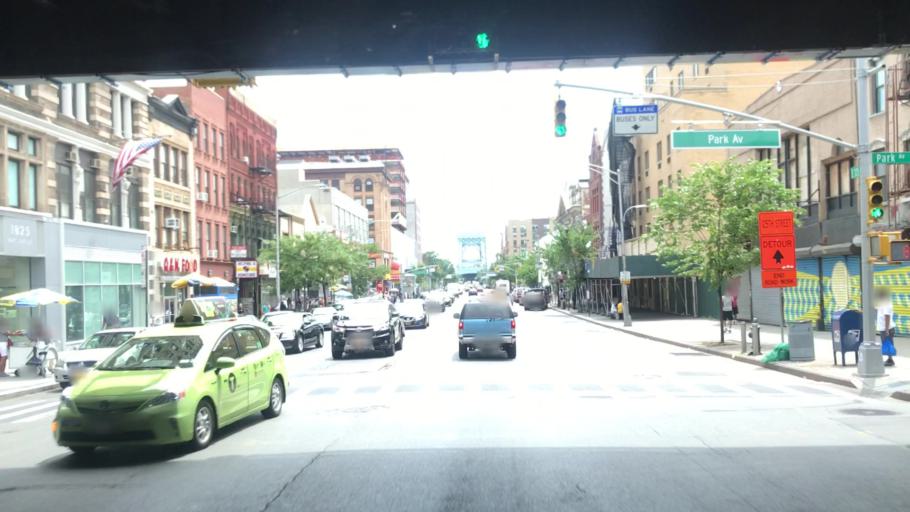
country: US
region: New York
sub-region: New York County
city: Manhattan
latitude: 40.8050
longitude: -73.9389
